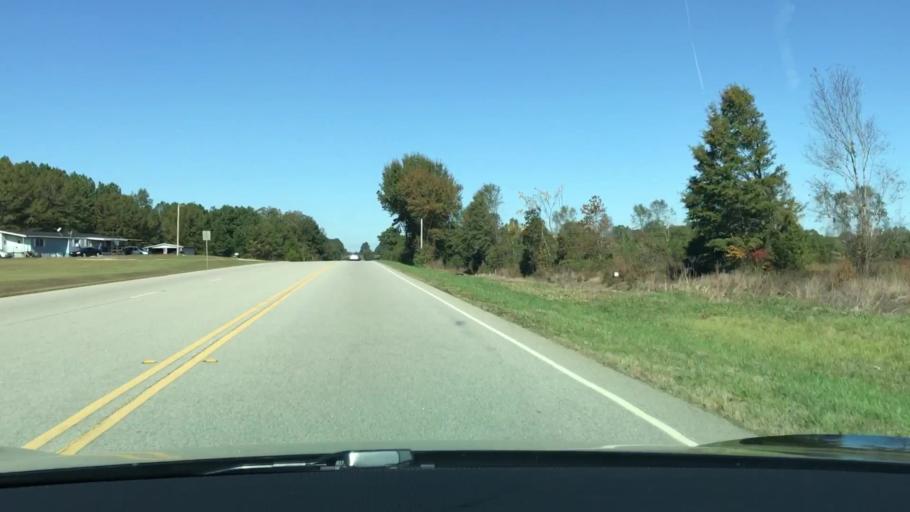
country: US
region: Georgia
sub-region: Taliaferro County
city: Crawfordville
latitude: 33.4908
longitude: -82.7982
